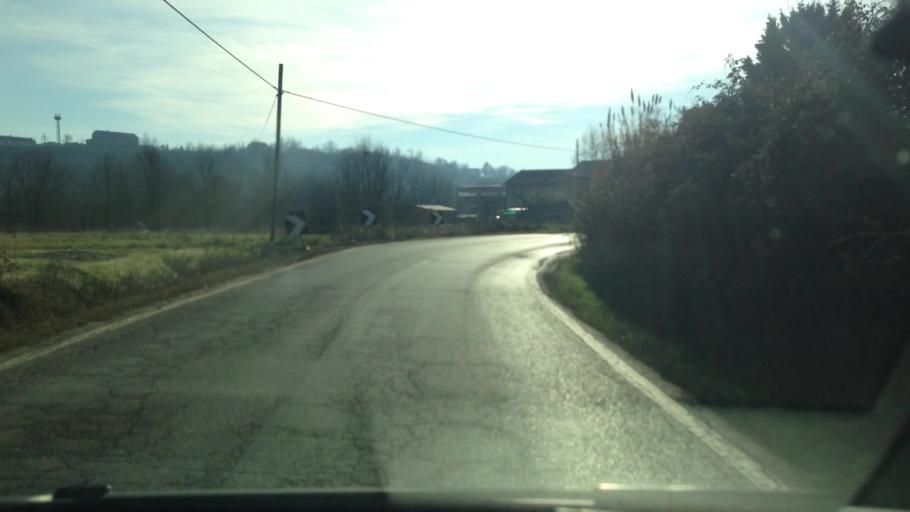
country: IT
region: Piedmont
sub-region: Provincia di Alessandria
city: Masio
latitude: 44.8655
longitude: 8.4165
